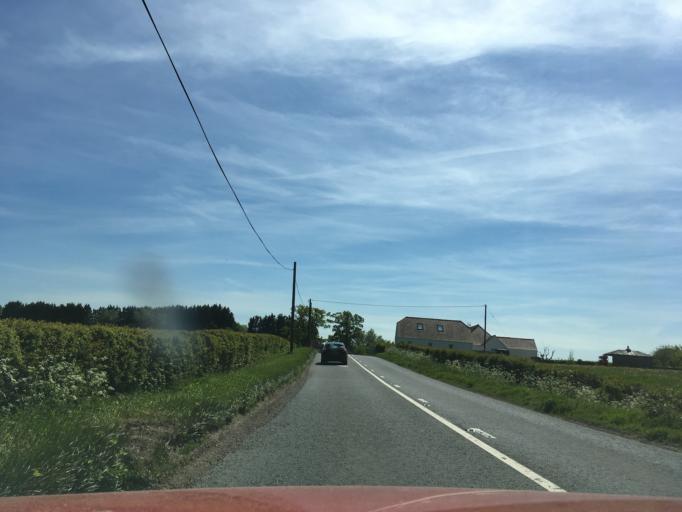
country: GB
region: England
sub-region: Wiltshire
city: Malmesbury
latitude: 51.5979
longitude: -2.0884
